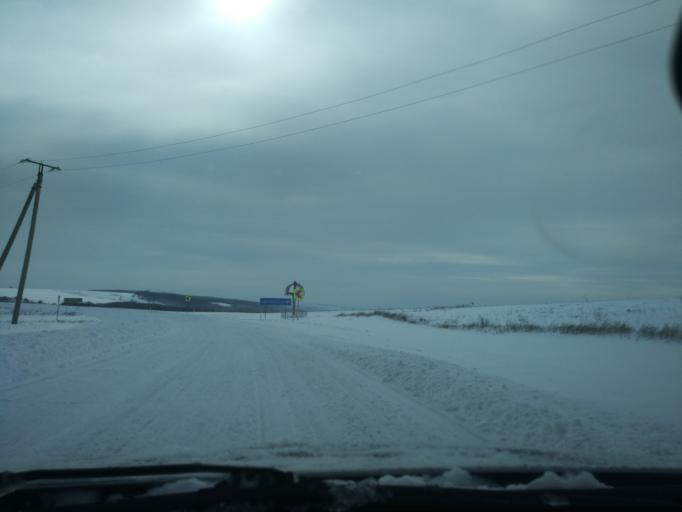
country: MD
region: Nisporeni
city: Nisporeni
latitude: 47.1240
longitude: 28.2070
